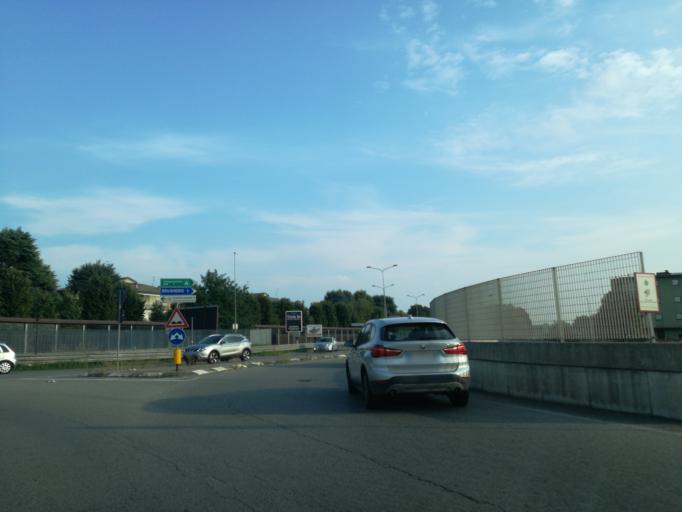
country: IT
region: Lombardy
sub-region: Citta metropolitana di Milano
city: Carugate
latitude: 45.5534
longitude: 9.3327
